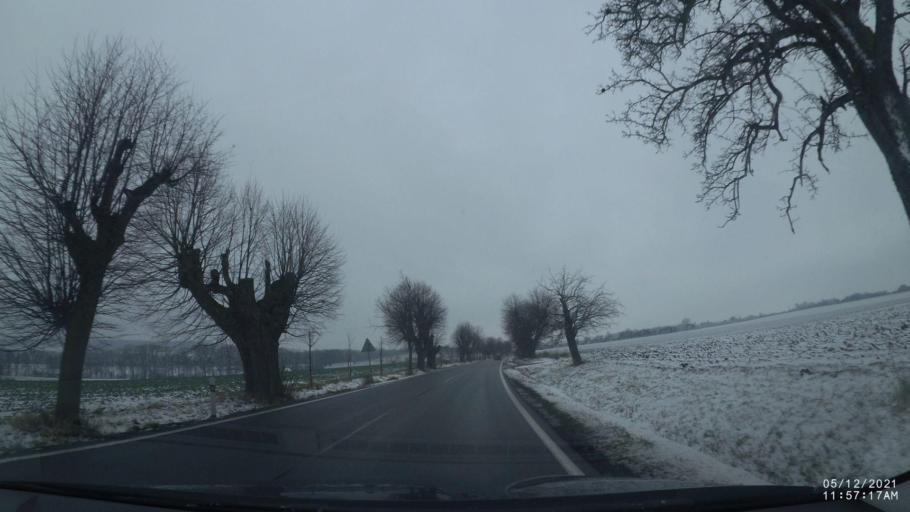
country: CZ
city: Dobruska
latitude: 50.2768
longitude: 16.1394
